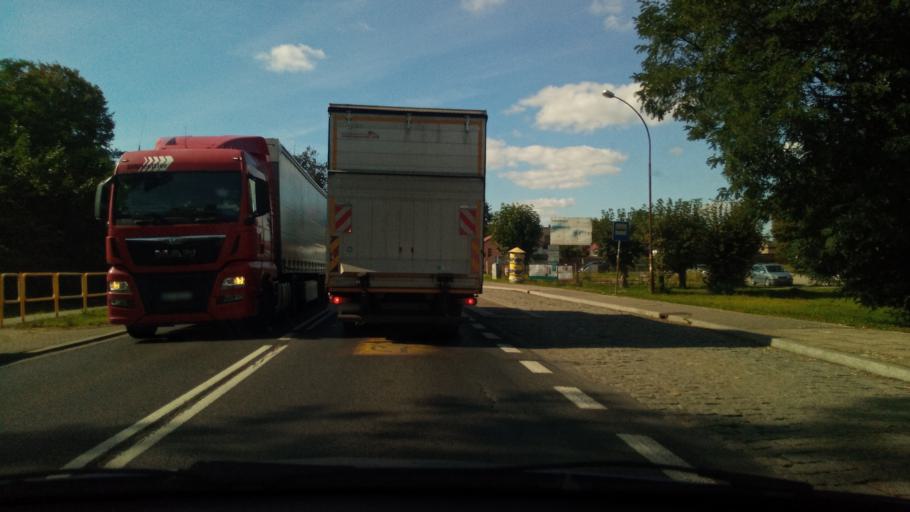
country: PL
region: Lodz Voivodeship
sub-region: Piotrkow Trybunalski
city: Piotrkow Trybunalski
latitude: 51.3927
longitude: 19.7687
